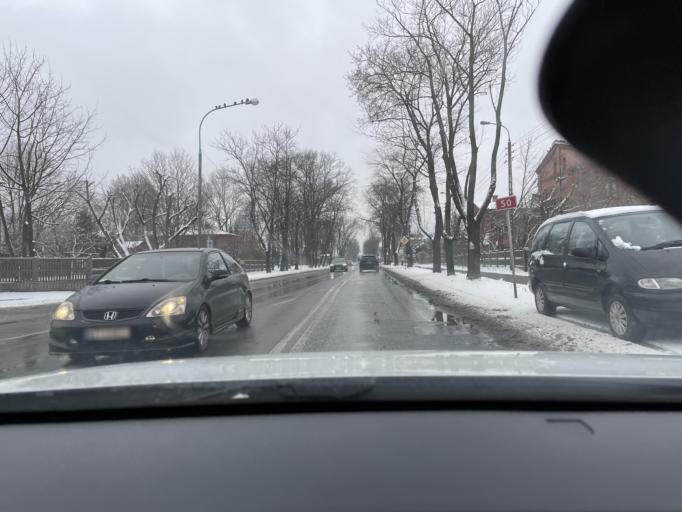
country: PL
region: Masovian Voivodeship
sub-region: Powiat zyrardowski
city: Zyrardow
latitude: 52.0483
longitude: 20.4463
